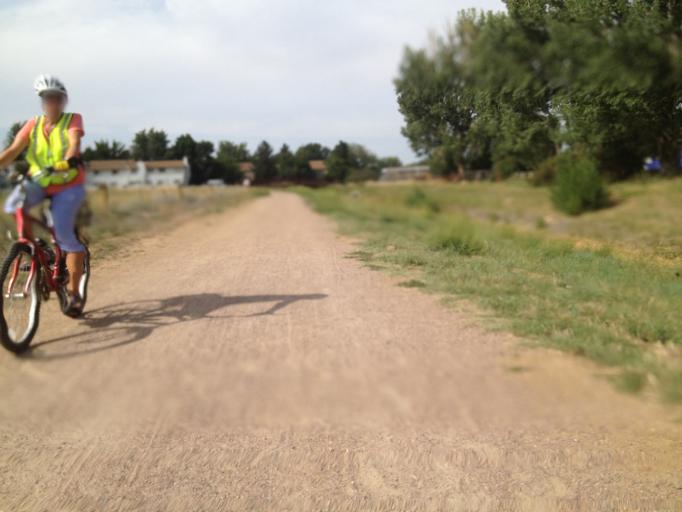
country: US
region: Colorado
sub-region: Boulder County
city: Louisville
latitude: 39.9820
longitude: -105.1142
